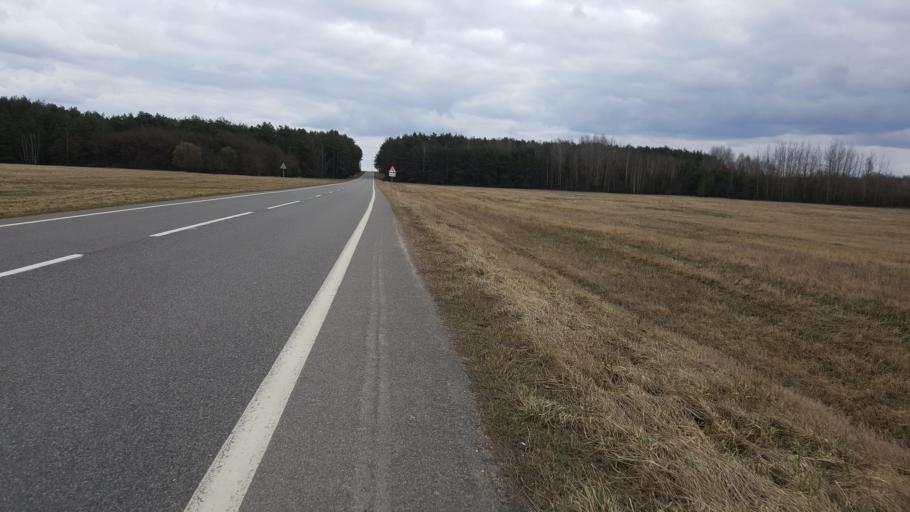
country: BY
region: Brest
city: Kamyanyuki
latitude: 52.4804
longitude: 23.8037
